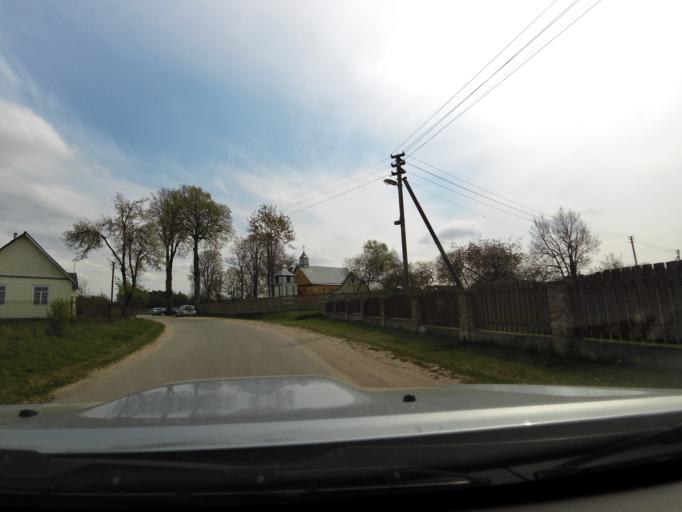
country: LT
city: Baltoji Voke
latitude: 54.4331
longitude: 25.1501
